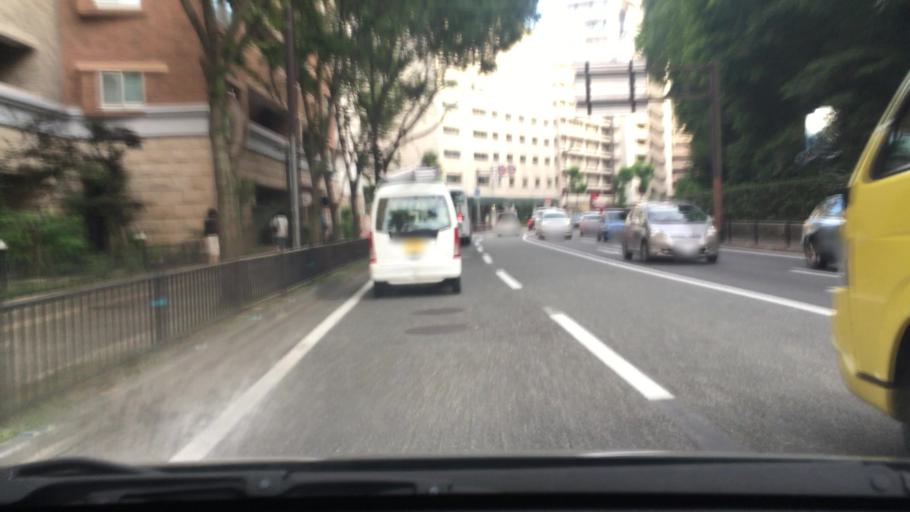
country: JP
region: Fukuoka
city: Fukuoka-shi
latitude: 33.5824
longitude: 130.3834
